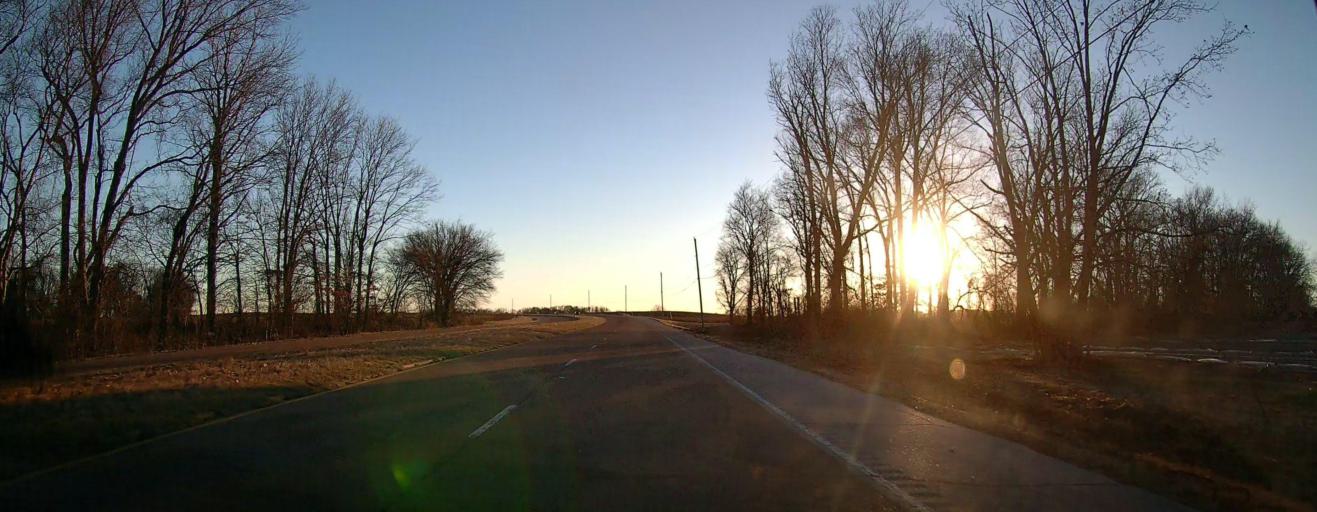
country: US
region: Tennessee
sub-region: Shelby County
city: Millington
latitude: 35.3122
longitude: -89.8787
